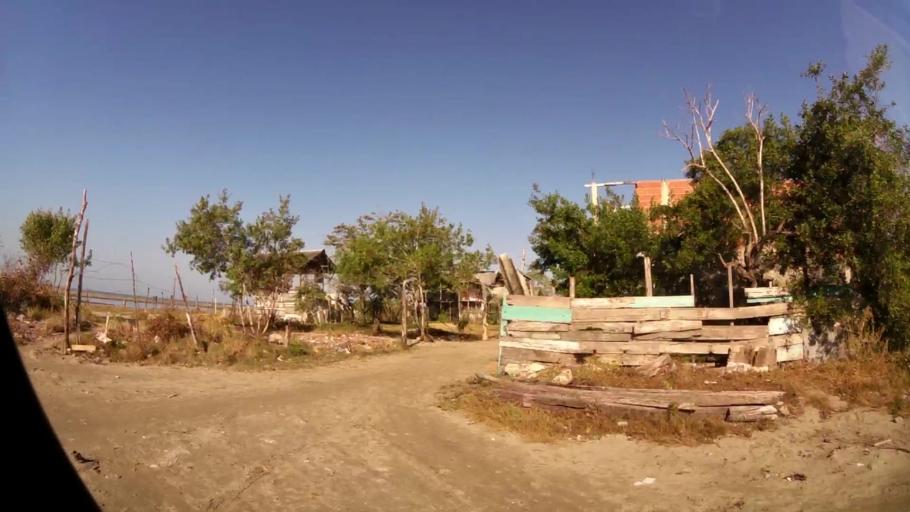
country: CO
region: Bolivar
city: Cartagena
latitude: 10.4966
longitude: -75.4975
